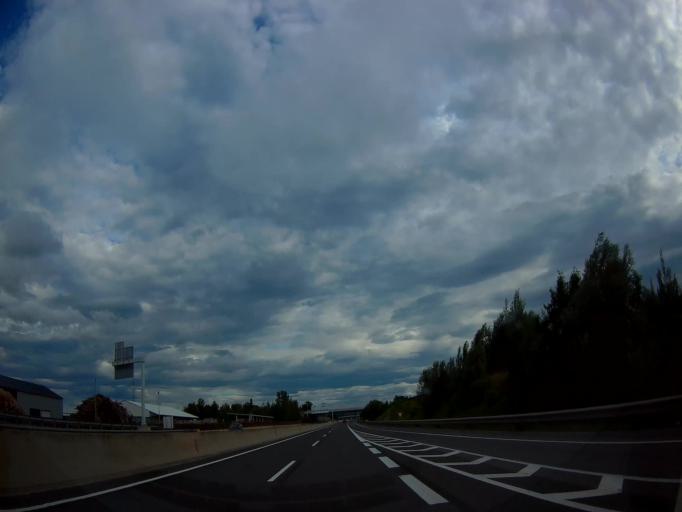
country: AT
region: Lower Austria
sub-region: Politischer Bezirk Sankt Polten
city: Traismauer
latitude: 48.3675
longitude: 15.7176
